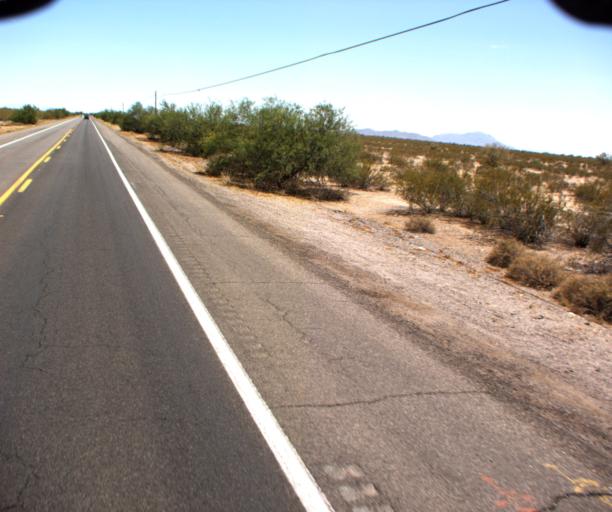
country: US
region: Arizona
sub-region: Pinal County
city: Florence
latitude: 33.0003
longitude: -111.3701
